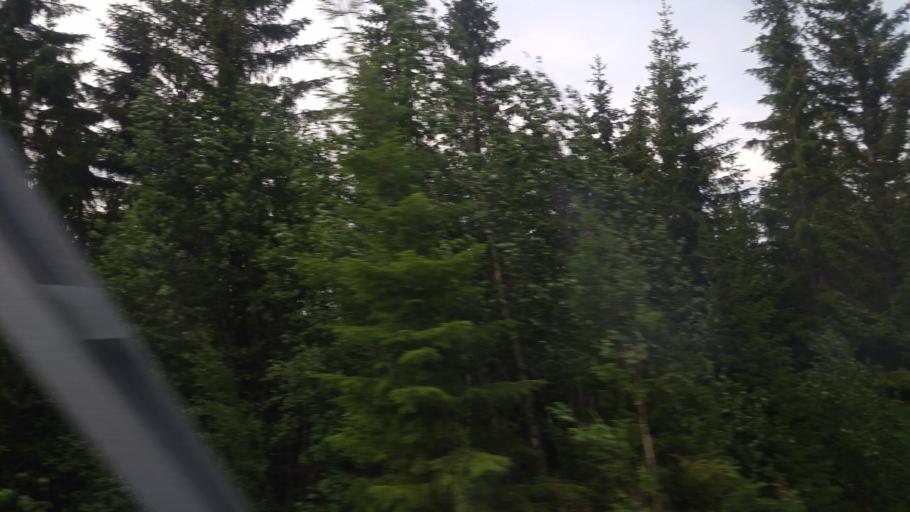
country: SE
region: Jaemtland
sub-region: Are Kommun
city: Are
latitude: 63.3964
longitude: 12.8087
